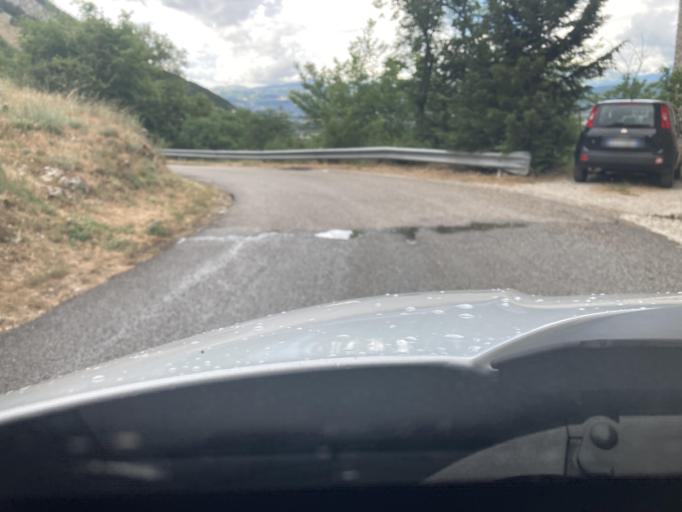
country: IT
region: Abruzzo
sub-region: Provincia dell' Aquila
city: Fossa
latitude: 42.2844
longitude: 13.4945
